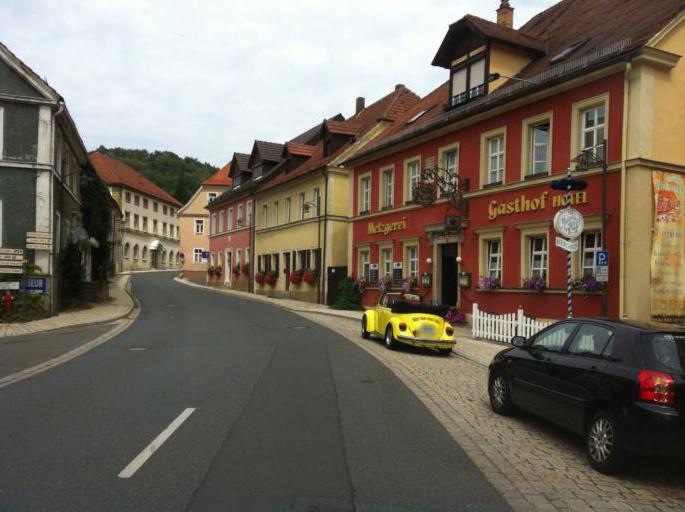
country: DE
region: Bavaria
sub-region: Upper Franconia
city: Goldkronach
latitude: 50.0075
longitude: 11.6848
